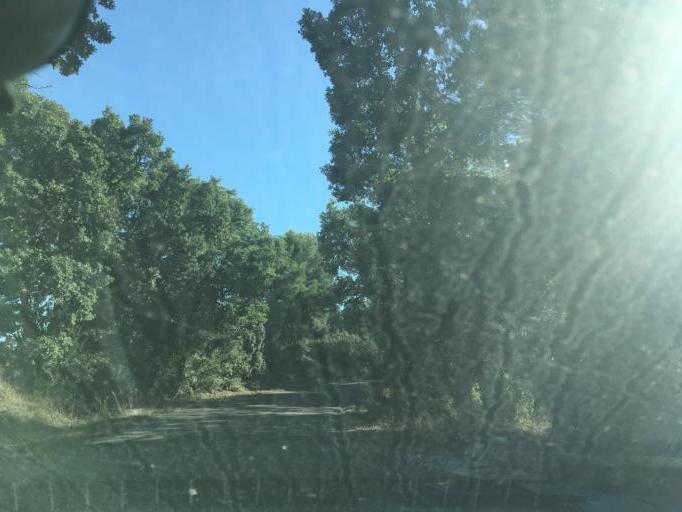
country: FR
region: Provence-Alpes-Cote d'Azur
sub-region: Departement du Var
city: Regusse
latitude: 43.7086
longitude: 6.1431
